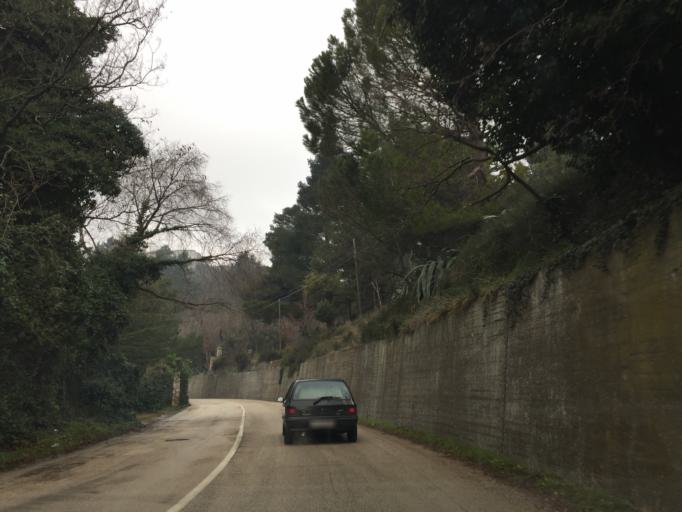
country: IT
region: Apulia
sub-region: Provincia di Foggia
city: Bovino
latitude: 41.2526
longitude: 15.3475
